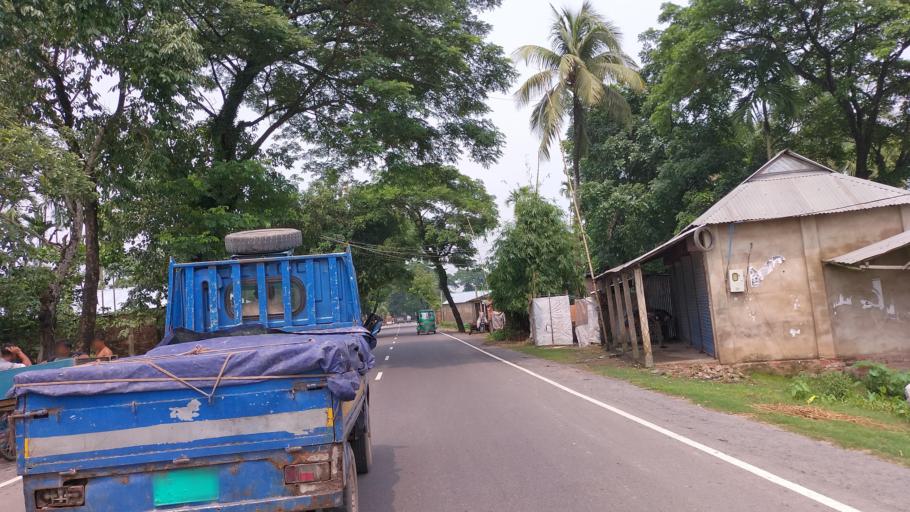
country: BD
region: Dhaka
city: Netrakona
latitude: 24.9019
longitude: 90.7582
